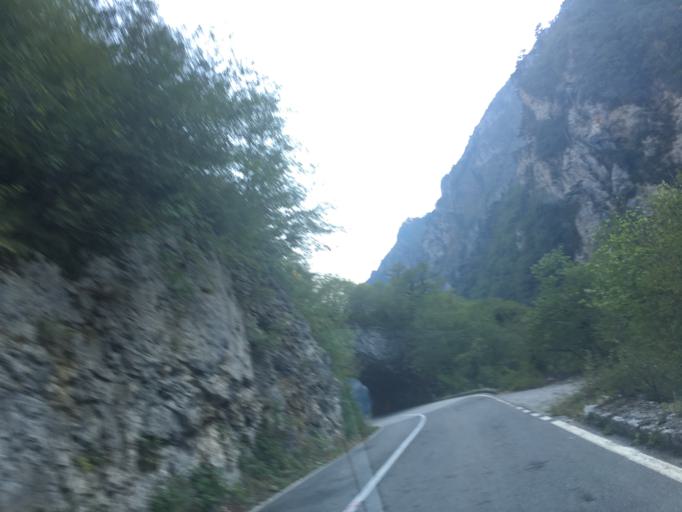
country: ME
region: Opstina Pluzine
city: Pluzine
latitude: 43.2979
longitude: 18.8535
